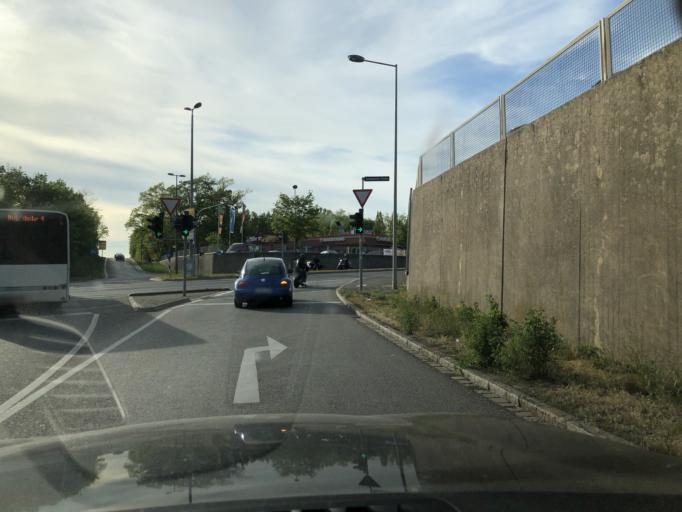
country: DE
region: Bavaria
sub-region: Regierungsbezirk Mittelfranken
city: Furth
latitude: 49.4524
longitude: 10.9898
